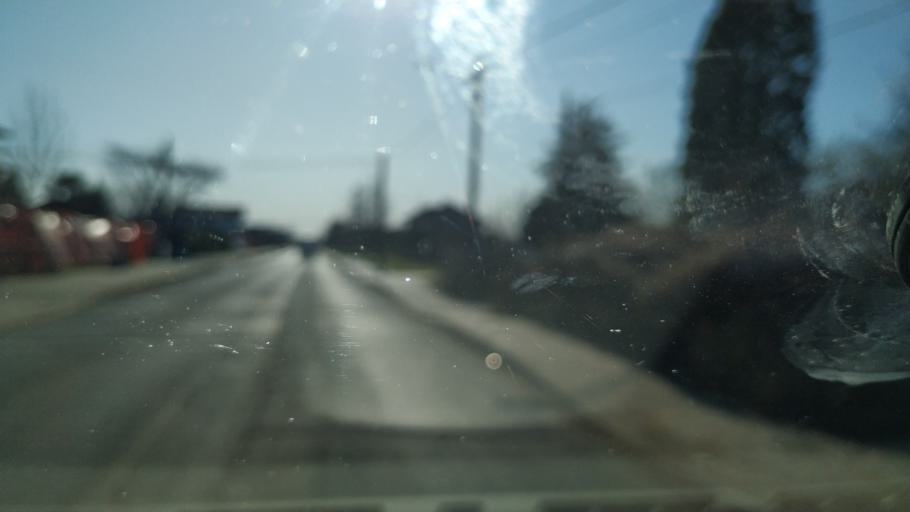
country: IT
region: Piedmont
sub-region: Provincia di Vercelli
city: Lozzolo
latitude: 45.6169
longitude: 8.3230
